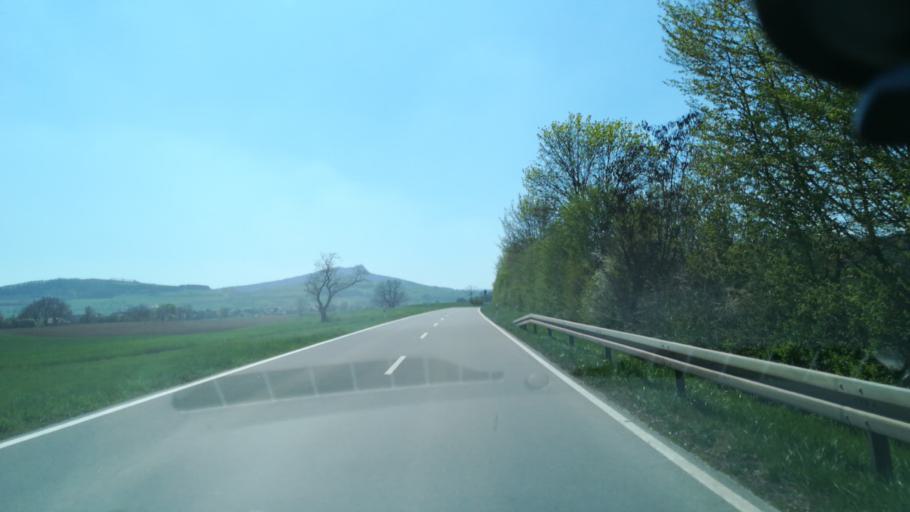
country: DE
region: Baden-Wuerttemberg
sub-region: Freiburg Region
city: Muhlhausen-Ehingen
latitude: 47.8384
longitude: 8.8118
